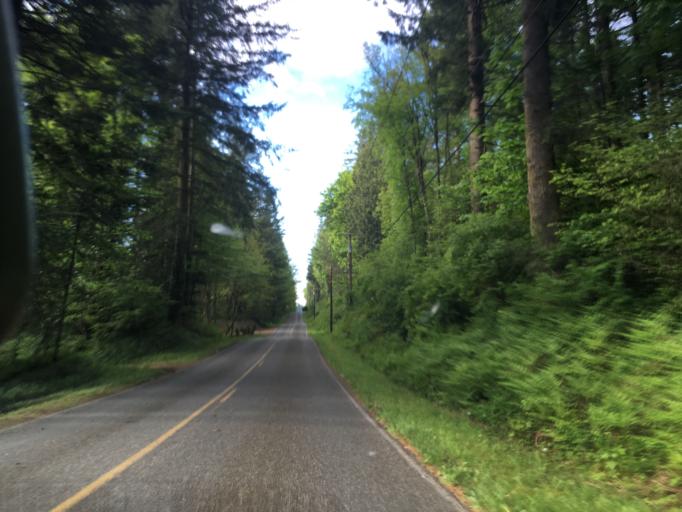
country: US
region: Washington
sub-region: Whatcom County
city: Sudden Valley
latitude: 48.7617
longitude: -122.3553
